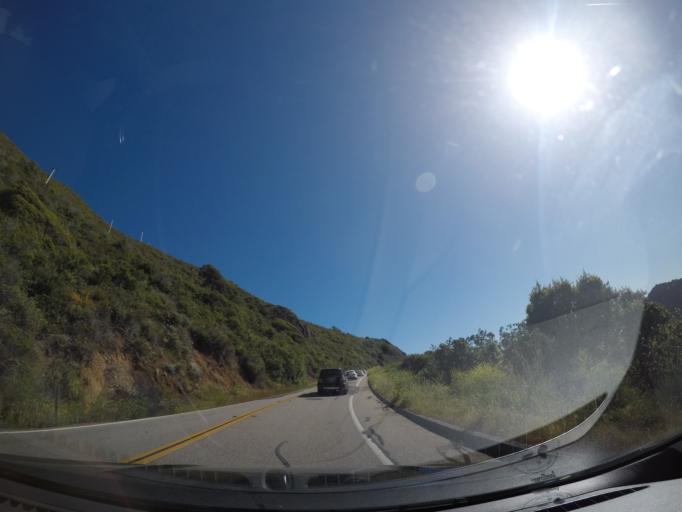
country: US
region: California
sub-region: San Luis Obispo County
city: Cambria
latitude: 35.8108
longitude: -121.3590
